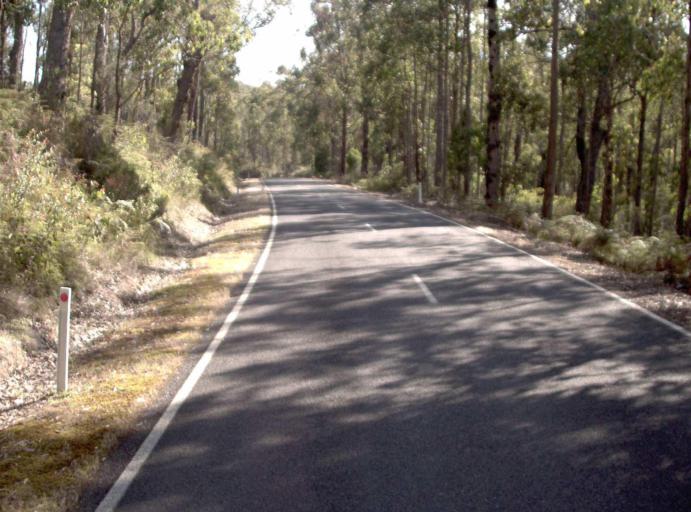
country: AU
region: Victoria
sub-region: East Gippsland
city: Lakes Entrance
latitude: -37.5755
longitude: 148.5475
